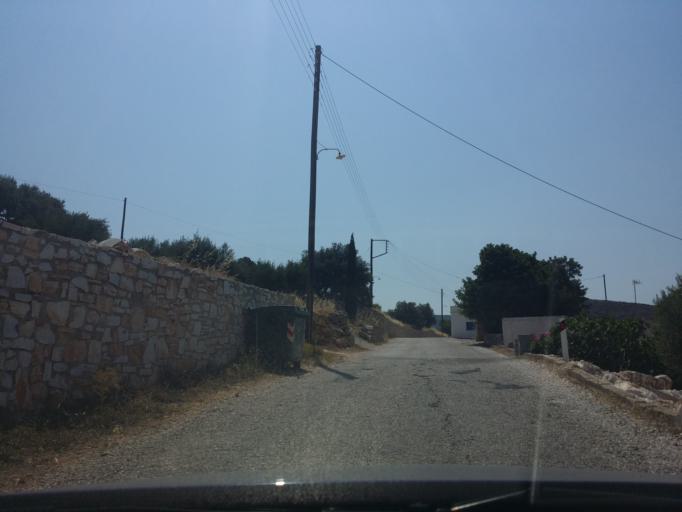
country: GR
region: South Aegean
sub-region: Nomos Kykladon
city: Antiparos
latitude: 37.0158
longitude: 25.1436
